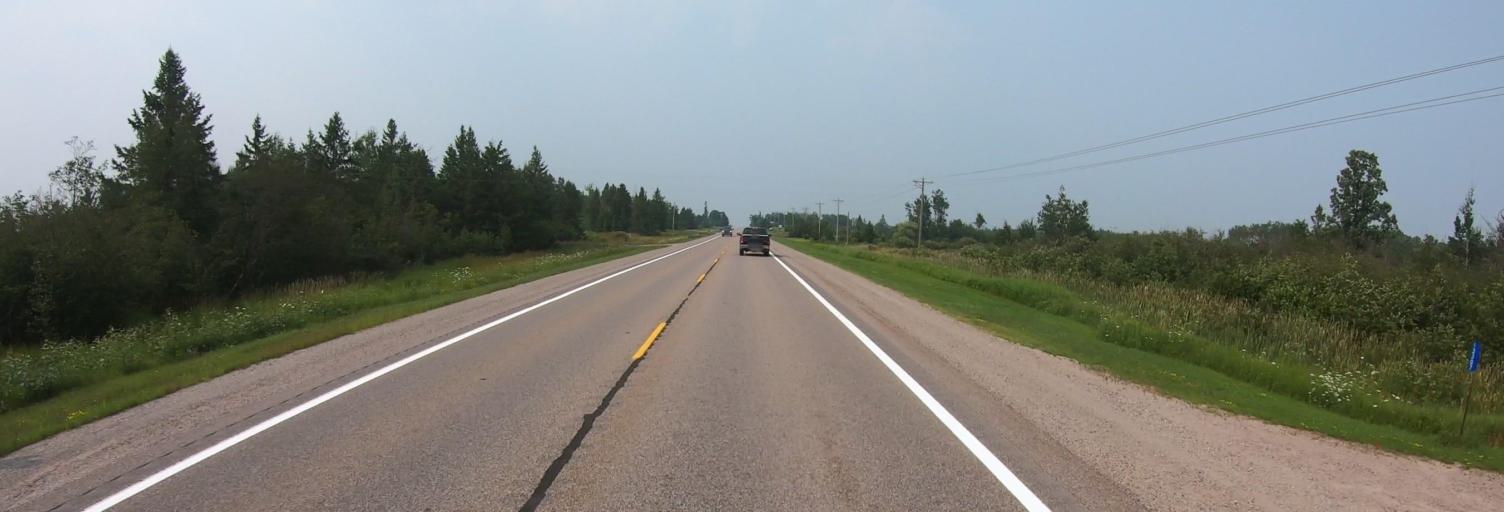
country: US
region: Michigan
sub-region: Chippewa County
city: Sault Ste. Marie
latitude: 46.3118
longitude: -84.3638
